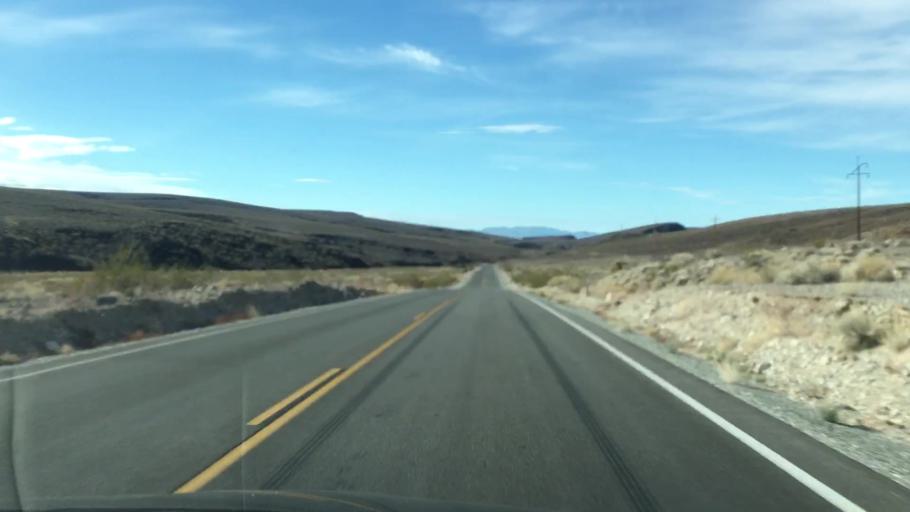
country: US
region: Nevada
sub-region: Nye County
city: Beatty
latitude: 36.3501
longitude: -116.6320
